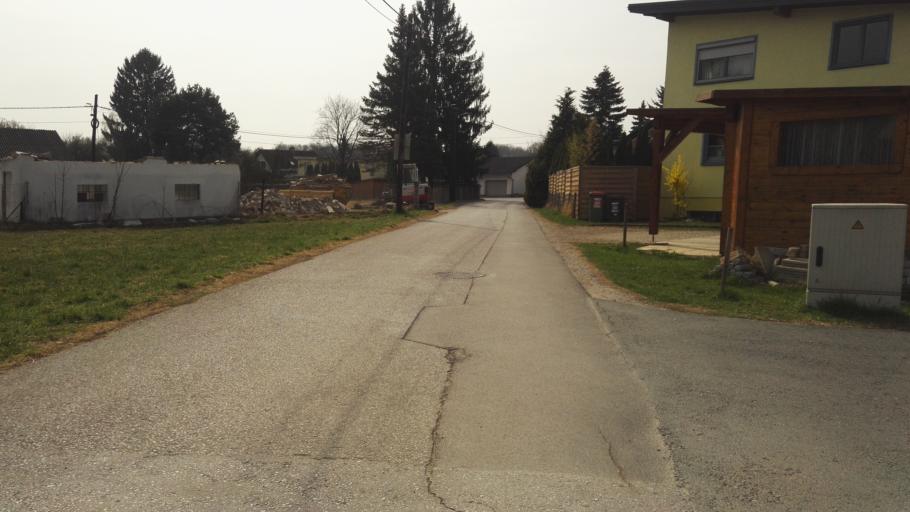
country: AT
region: Styria
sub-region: Politischer Bezirk Graz-Umgebung
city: Feldkirchen bei Graz
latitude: 47.0218
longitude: 15.4520
